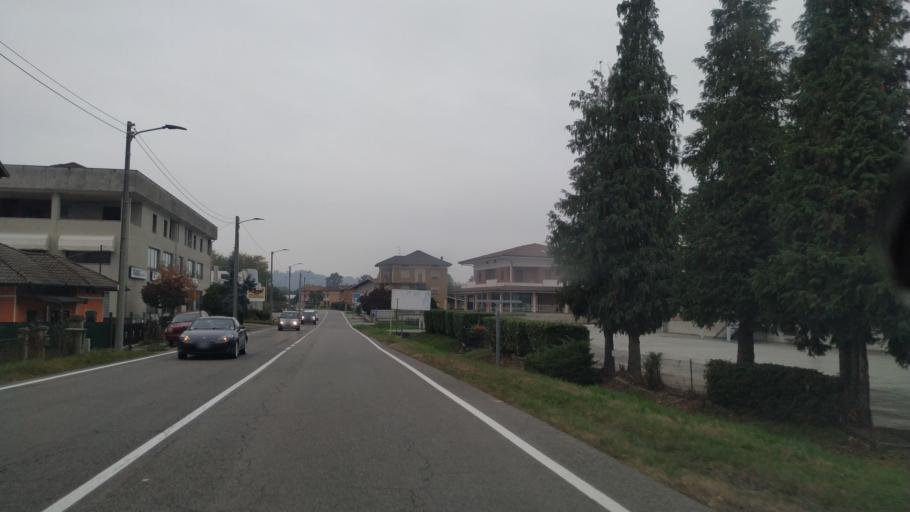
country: IT
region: Piedmont
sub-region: Provincia di Biella
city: Cerreto Castello
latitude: 45.5611
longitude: 8.1731
